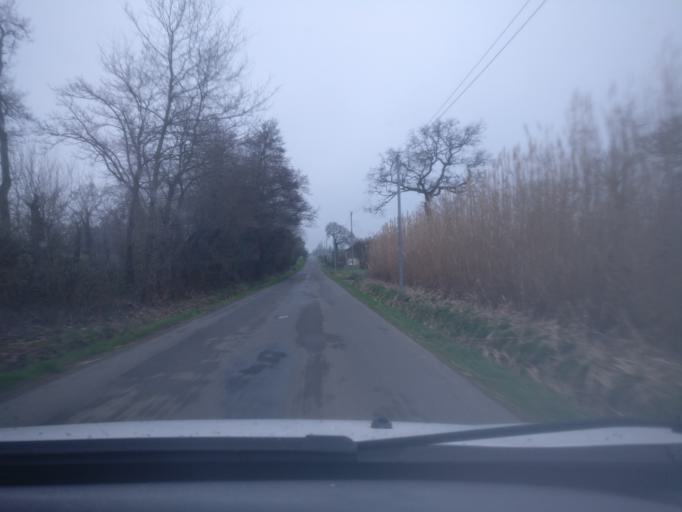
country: FR
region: Brittany
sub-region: Departement d'Ille-et-Vilaine
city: Montreuil-sur-Ille
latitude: 48.3030
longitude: -1.6357
